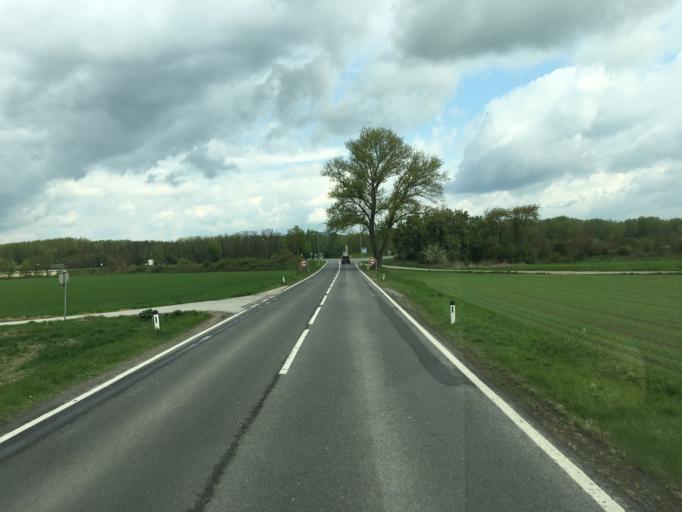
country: AT
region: Lower Austria
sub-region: Politischer Bezirk Bruck an der Leitha
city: Berg
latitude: 48.1251
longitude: 17.0309
